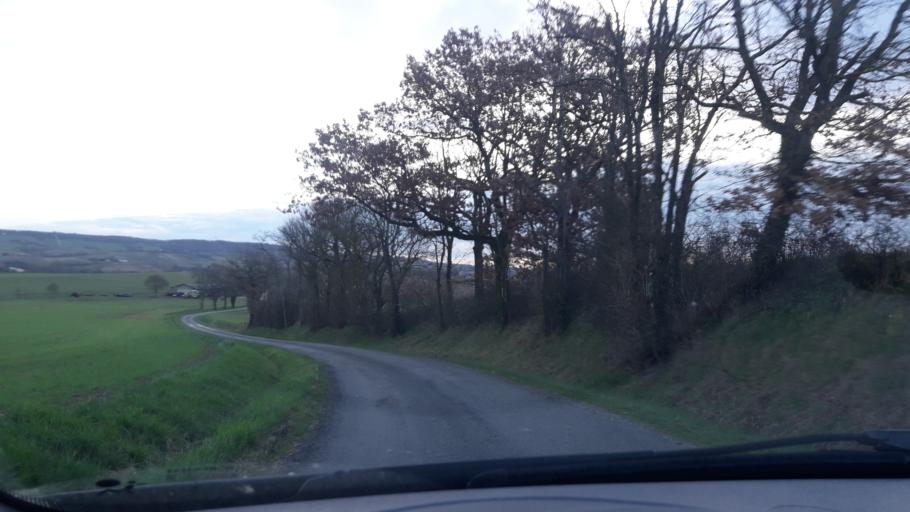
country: FR
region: Midi-Pyrenees
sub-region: Departement du Gers
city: Pujaudran
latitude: 43.6653
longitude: 1.0640
